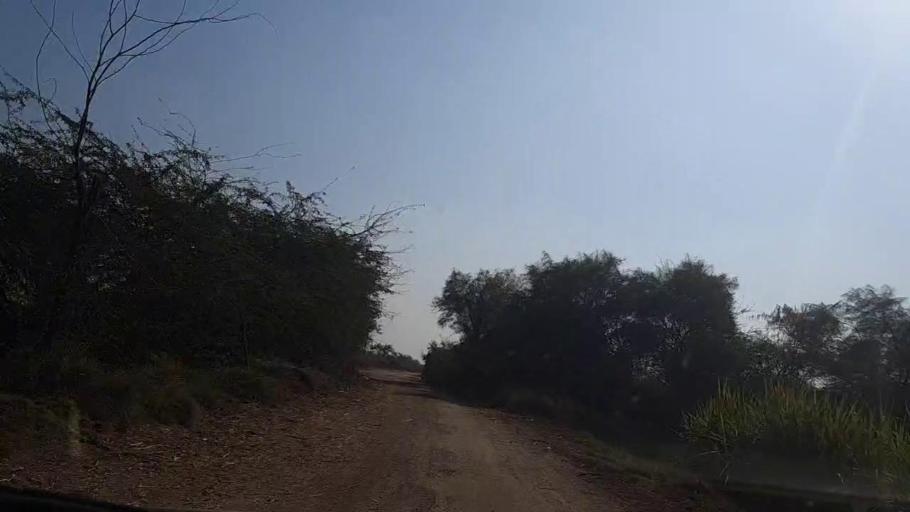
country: PK
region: Sindh
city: Sakrand
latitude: 26.0749
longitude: 68.3694
